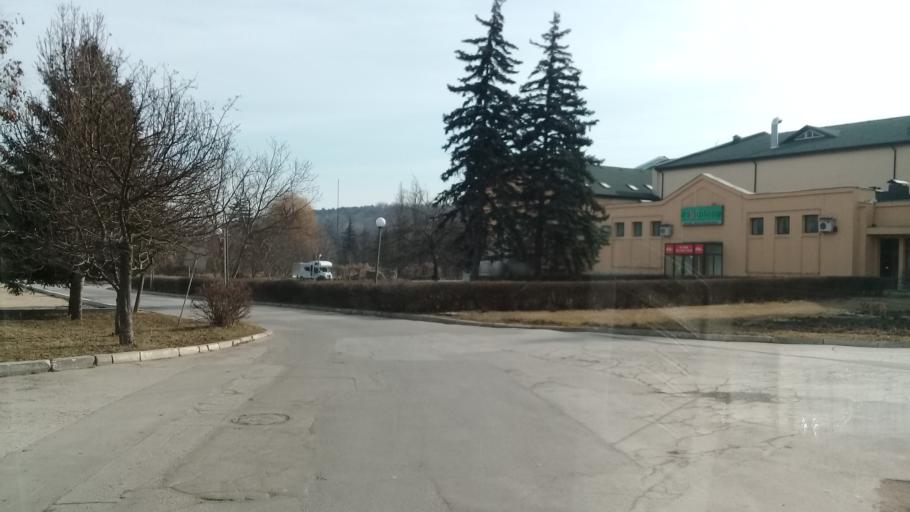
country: MD
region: Chisinau
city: Chisinau
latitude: 47.0168
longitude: 28.8032
